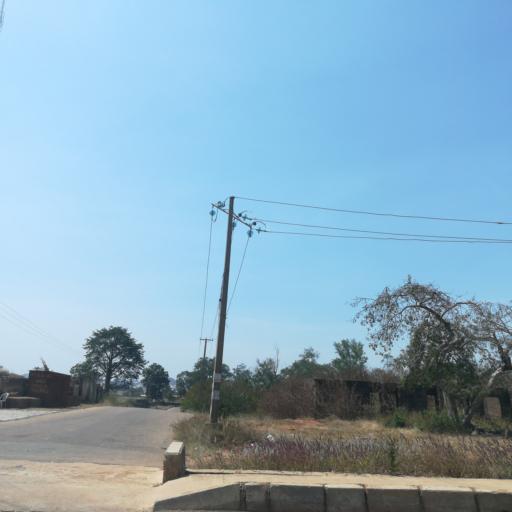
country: NG
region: Plateau
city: Bukuru
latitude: 9.8444
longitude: 8.9007
